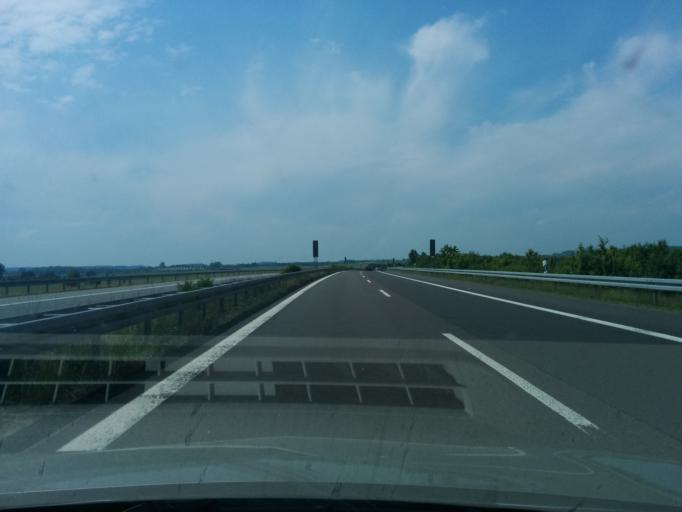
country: DE
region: Mecklenburg-Vorpommern
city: Strasburg
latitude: 53.5177
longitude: 13.7905
